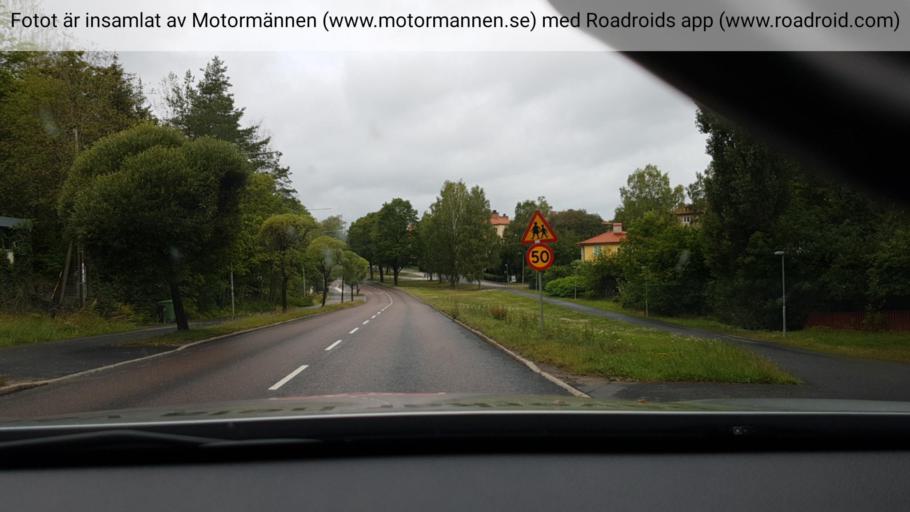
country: SE
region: Stockholm
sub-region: Lidingo
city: Lidingoe
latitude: 59.3637
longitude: 18.1427
